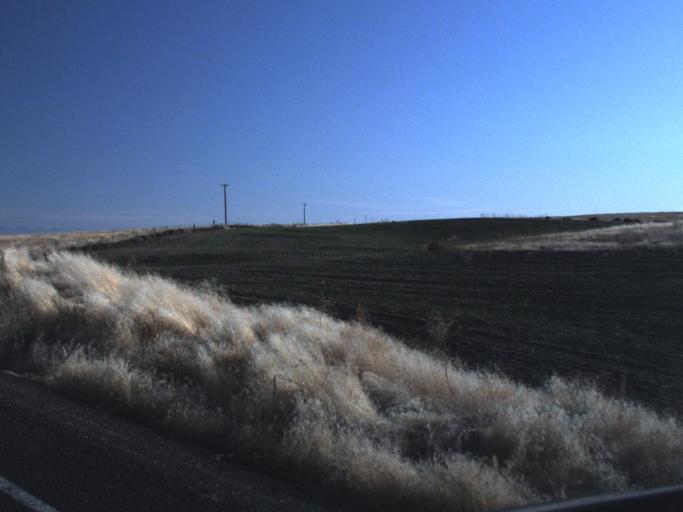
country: US
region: Washington
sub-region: Adams County
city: Ritzville
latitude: 46.7947
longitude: -118.2956
